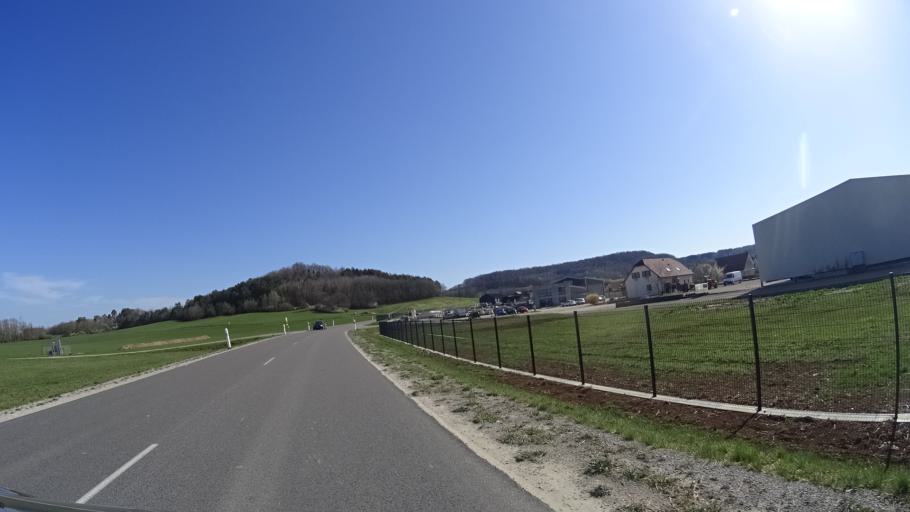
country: FR
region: Franche-Comte
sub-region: Departement du Doubs
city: Saone
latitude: 47.1591
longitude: 6.1006
